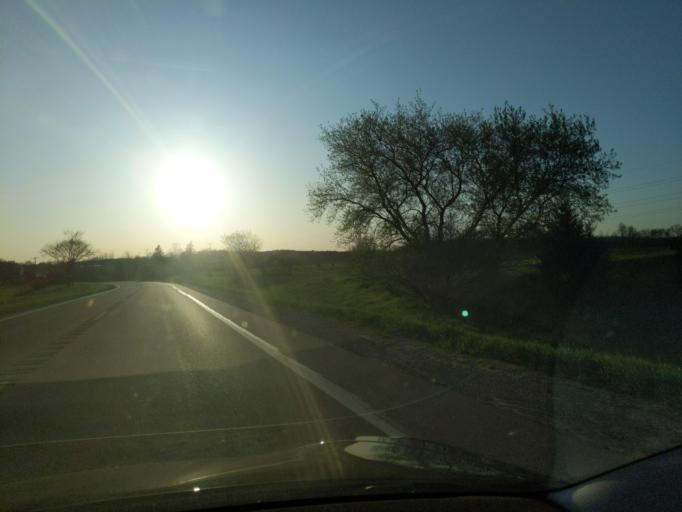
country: US
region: Michigan
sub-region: Ingham County
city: Stockbridge
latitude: 42.4186
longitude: -84.1546
